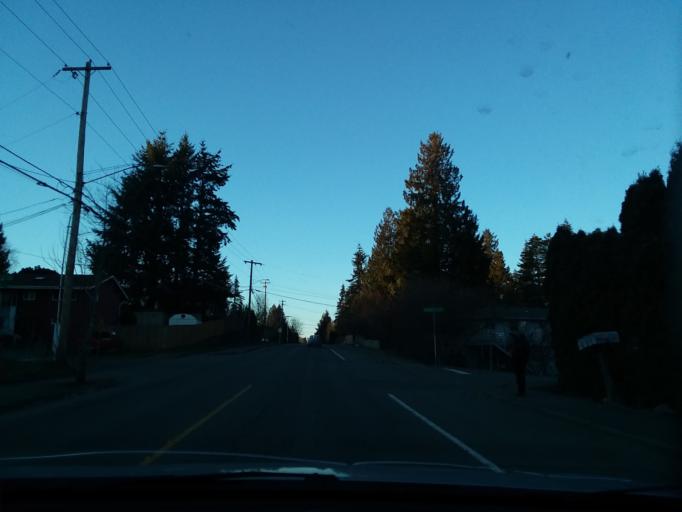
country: US
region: Washington
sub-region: Snohomish County
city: Mountlake Terrace
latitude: 47.7817
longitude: -122.2976
